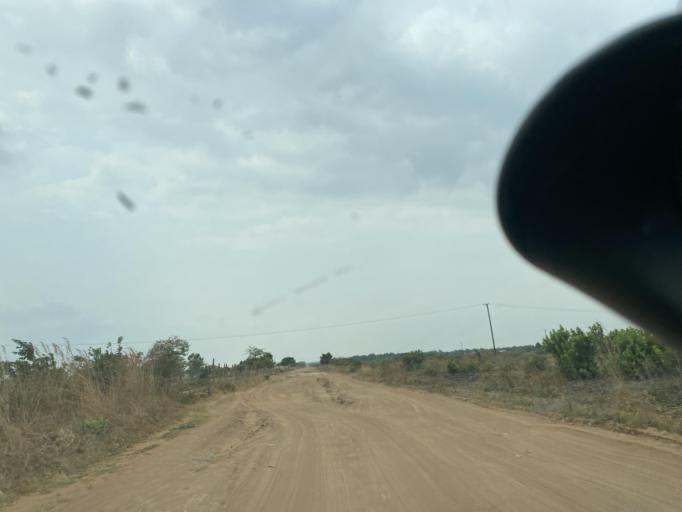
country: ZM
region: Lusaka
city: Lusaka
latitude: -15.2170
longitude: 28.3381
